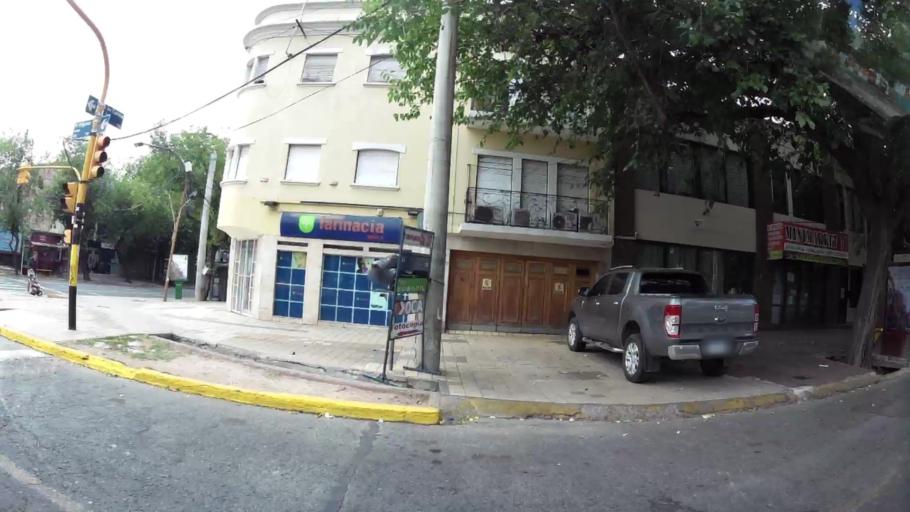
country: AR
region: Mendoza
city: Mendoza
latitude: -32.8933
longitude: -68.8508
